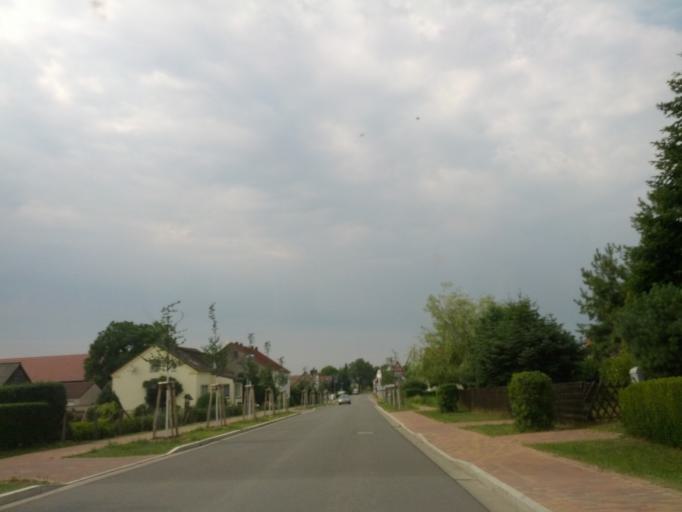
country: DE
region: Brandenburg
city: Fehrbellin
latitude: 52.7768
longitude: 12.8353
